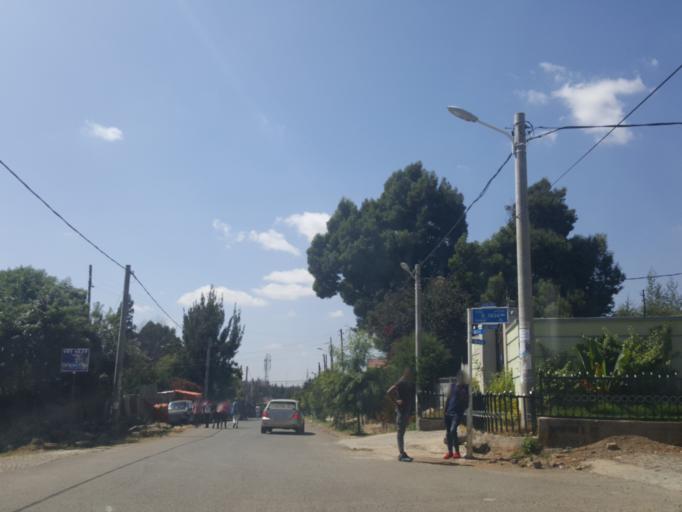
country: ET
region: Adis Abeba
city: Addis Ababa
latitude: 9.0544
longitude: 38.7355
